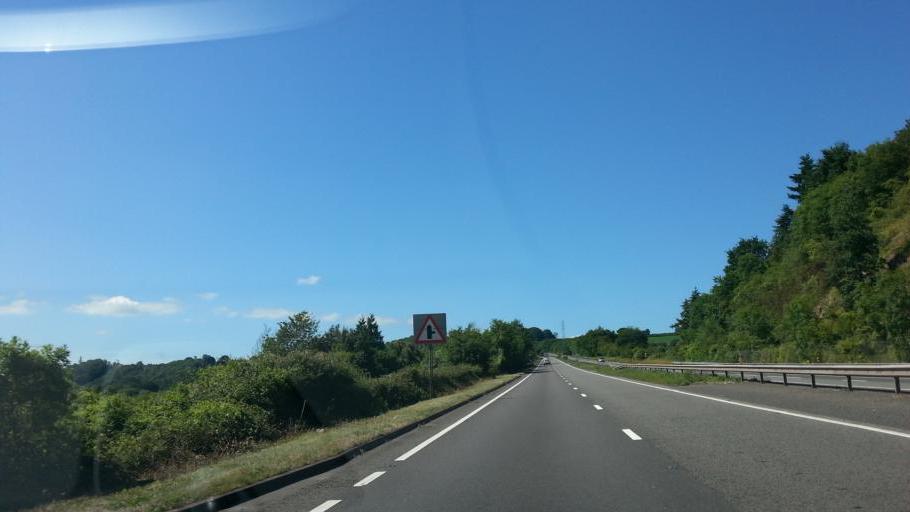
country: GB
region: England
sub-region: Herefordshire
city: Walford
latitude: 51.8975
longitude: -2.6308
